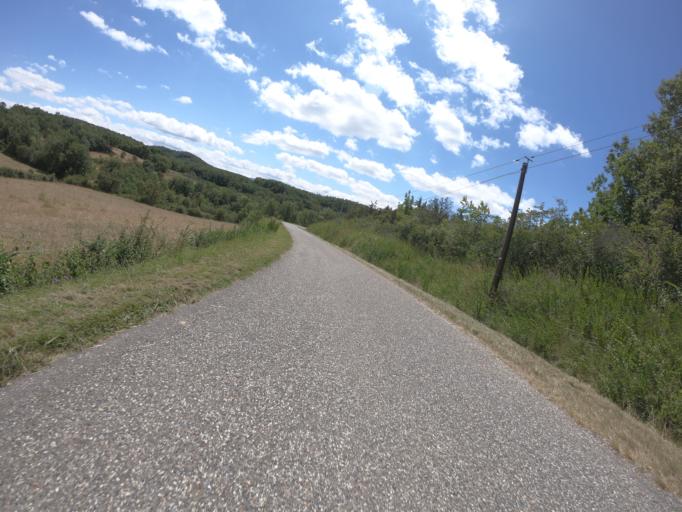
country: FR
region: Midi-Pyrenees
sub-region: Departement de l'Ariege
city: Mirepoix
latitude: 43.0482
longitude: 1.8325
